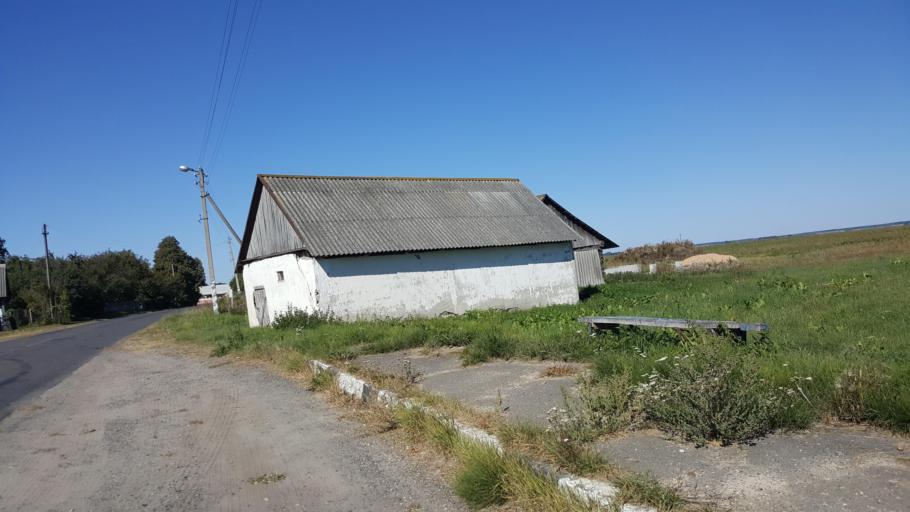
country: BY
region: Brest
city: Vysokaye
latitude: 52.2613
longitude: 23.5309
